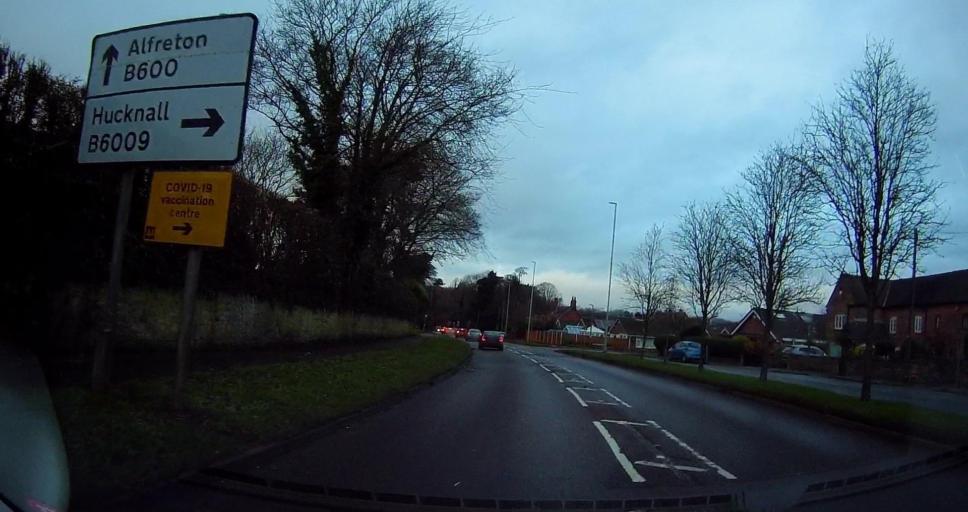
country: GB
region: England
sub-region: Nottinghamshire
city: Kimberley
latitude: 53.0100
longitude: -1.2561
